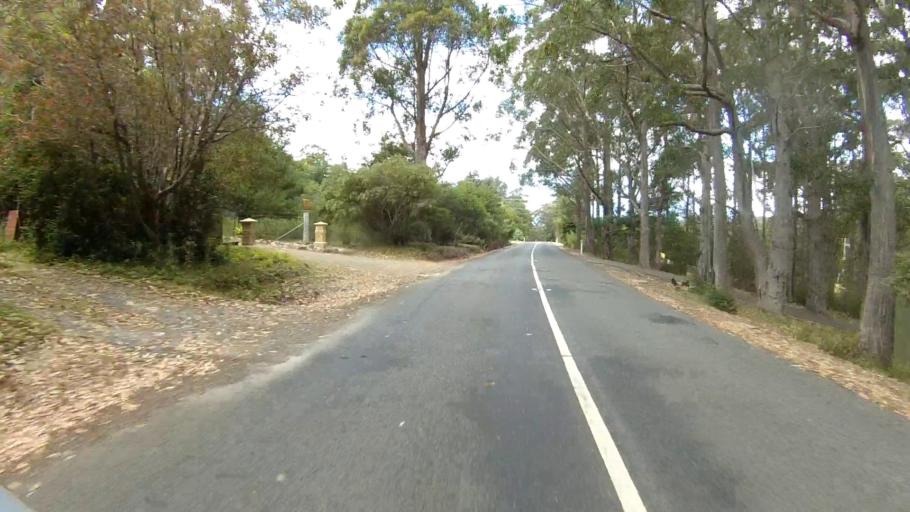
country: AU
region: Tasmania
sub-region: Kingborough
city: Margate
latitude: -42.9728
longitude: 147.1678
